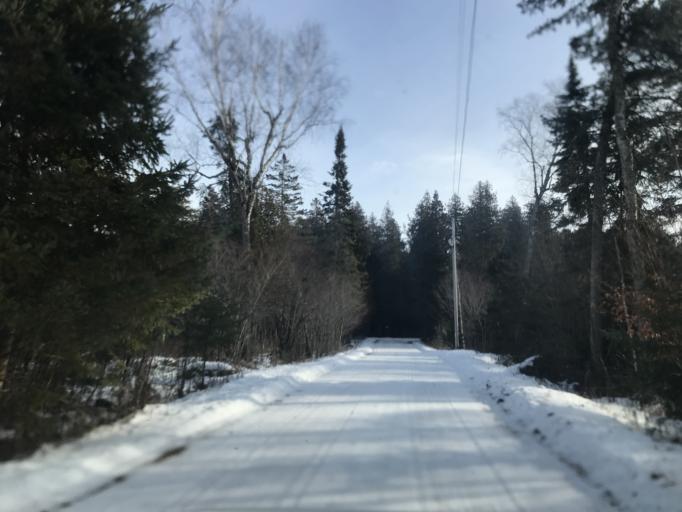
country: US
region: Wisconsin
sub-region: Door County
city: Sturgeon Bay
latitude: 45.1487
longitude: -87.0341
